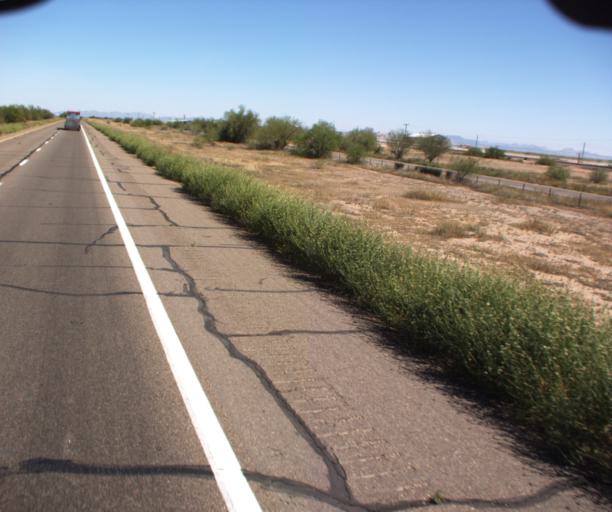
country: US
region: Arizona
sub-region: Maricopa County
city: Gila Bend
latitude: 32.9240
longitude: -112.8698
